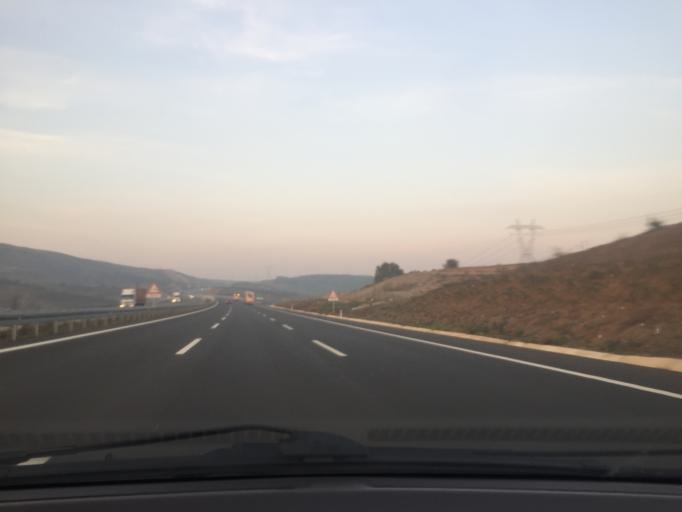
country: TR
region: Bursa
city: Mahmudiye
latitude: 40.2750
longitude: 28.5743
